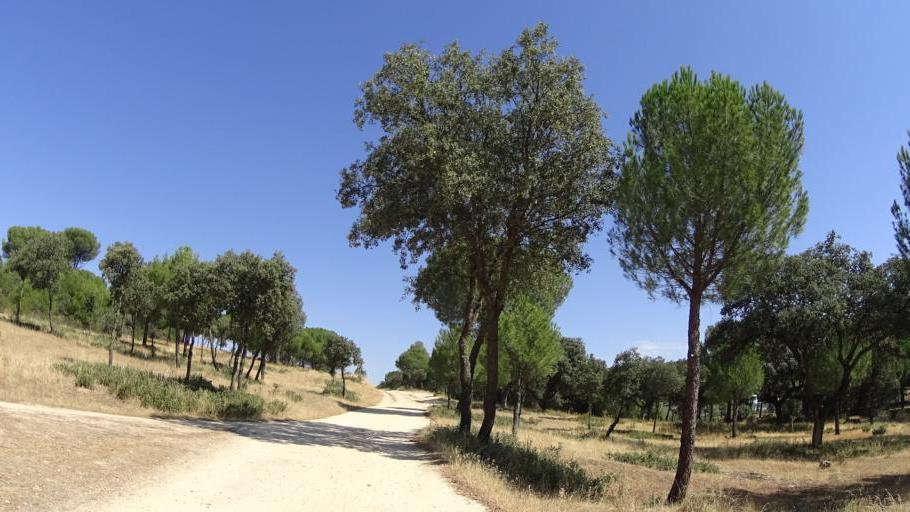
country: ES
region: Madrid
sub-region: Provincia de Madrid
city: Boadilla del Monte
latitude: 40.4263
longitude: -3.8540
